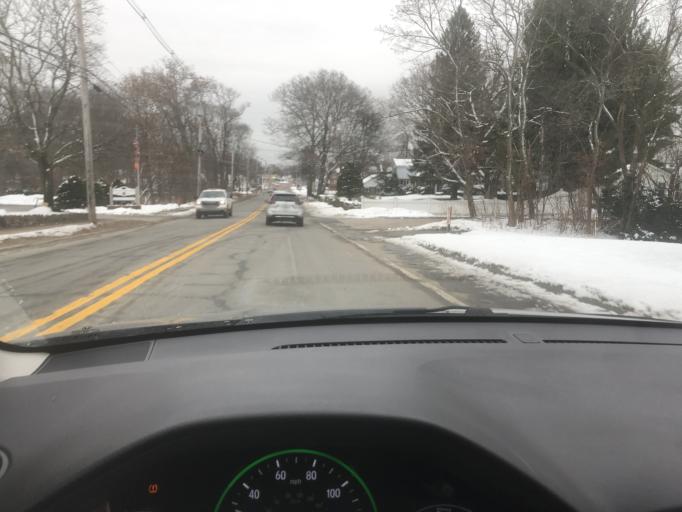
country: US
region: Massachusetts
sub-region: Middlesex County
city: Tewksbury
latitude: 42.6088
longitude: -71.2291
